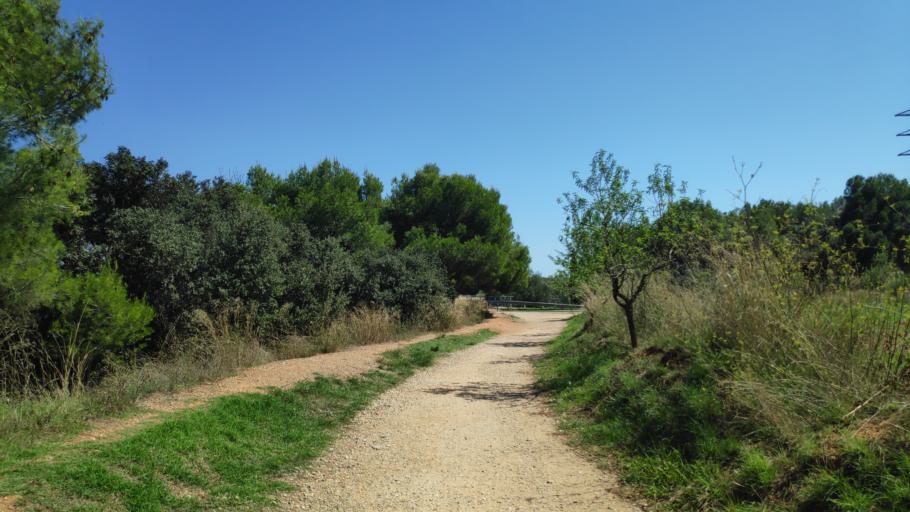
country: ES
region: Catalonia
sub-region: Provincia de Barcelona
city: Sant Quirze del Valles
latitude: 41.5448
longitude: 2.0766
